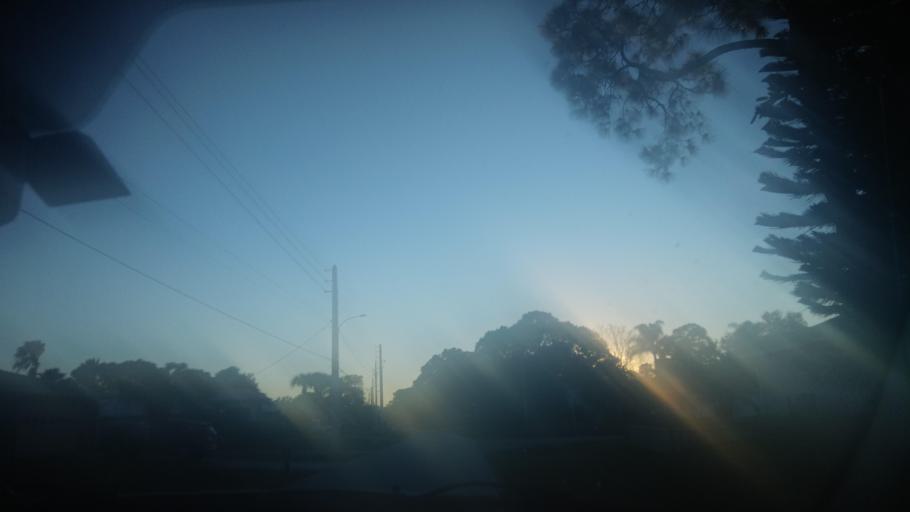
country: US
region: Florida
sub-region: Indian River County
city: Sebastian
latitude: 27.7641
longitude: -80.4787
